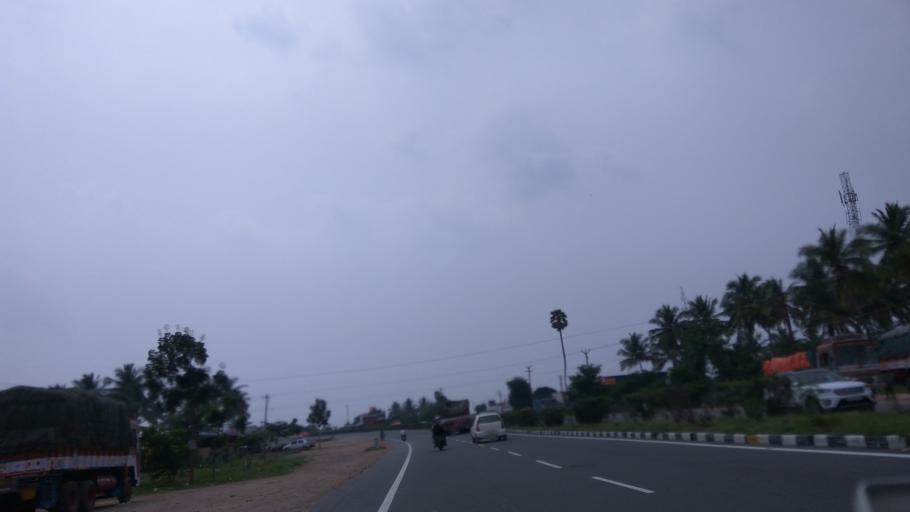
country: IN
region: Tamil Nadu
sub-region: Krishnagiri
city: Kaverippattanam
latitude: 12.3219
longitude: 78.2082
